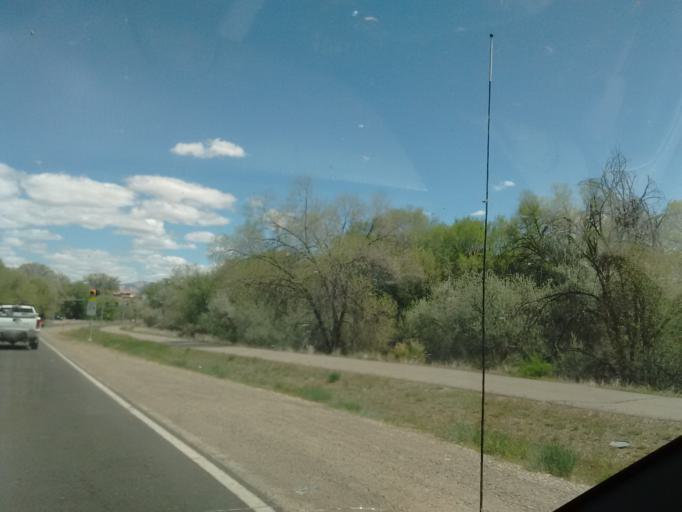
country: US
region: Colorado
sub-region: Mesa County
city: Redlands
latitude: 39.0801
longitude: -108.6330
